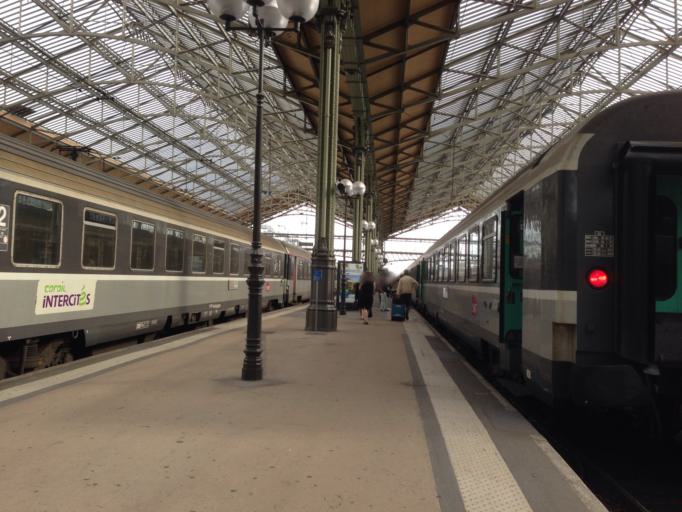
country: FR
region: Centre
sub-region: Departement d'Indre-et-Loire
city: Tours
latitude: 47.3894
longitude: 0.6940
